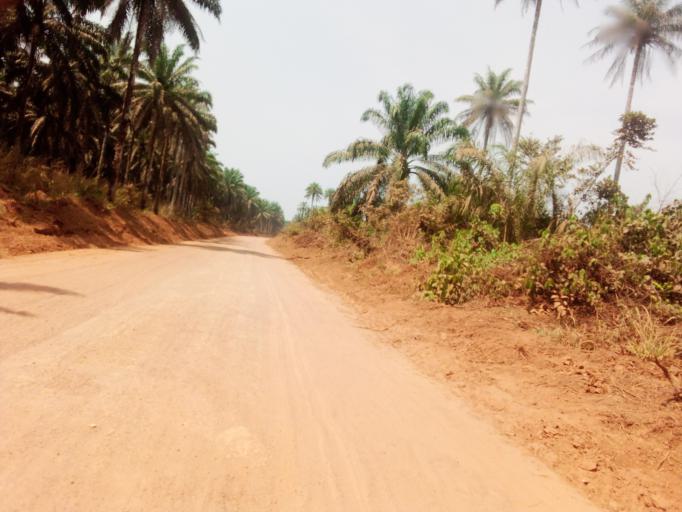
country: SL
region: Southern Province
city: Sumbuya
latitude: 7.6199
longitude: -12.1193
